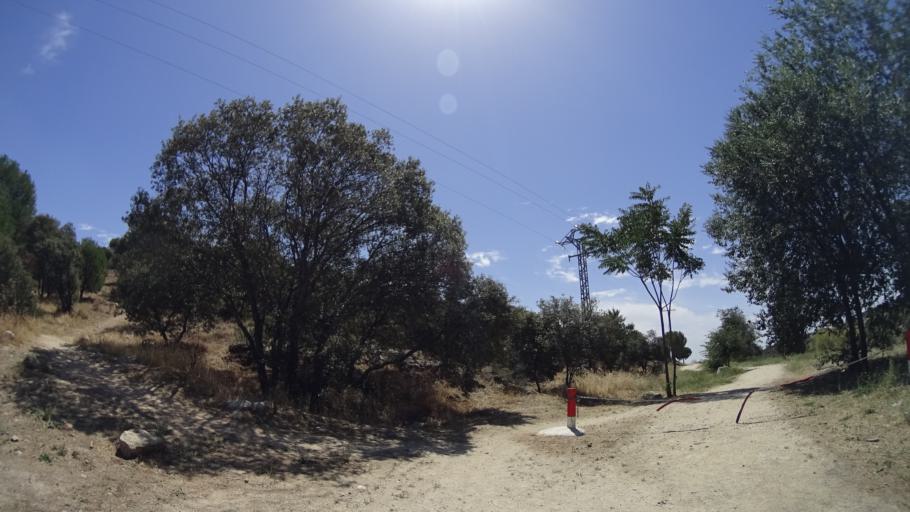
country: ES
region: Madrid
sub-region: Provincia de Madrid
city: Torrelodones
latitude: 40.5718
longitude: -3.9298
